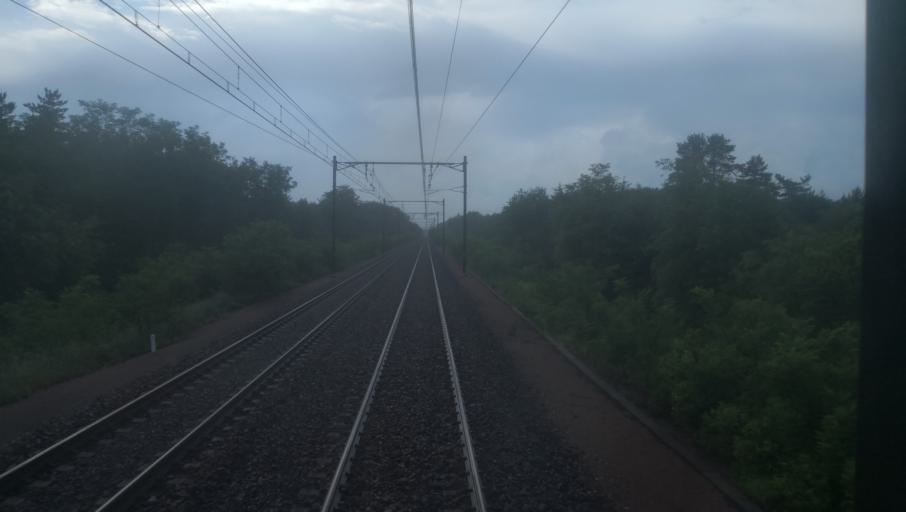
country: FR
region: Centre
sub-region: Departement du Loiret
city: La Ferte-Saint-Aubin
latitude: 47.6668
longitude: 1.9672
